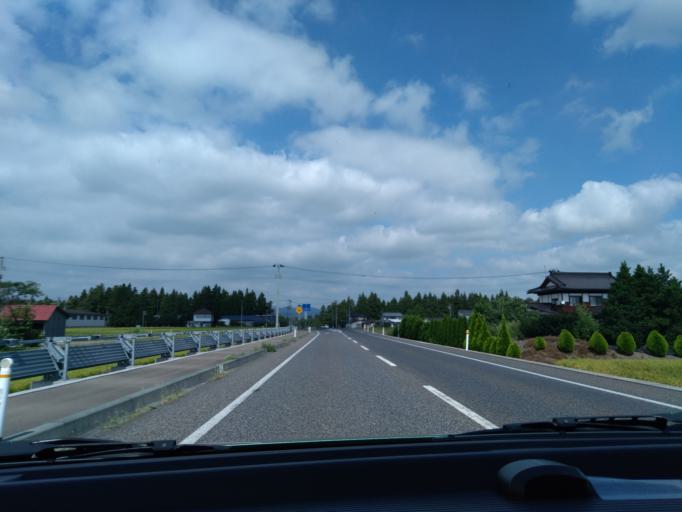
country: JP
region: Iwate
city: Hanamaki
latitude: 39.3717
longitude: 141.0570
